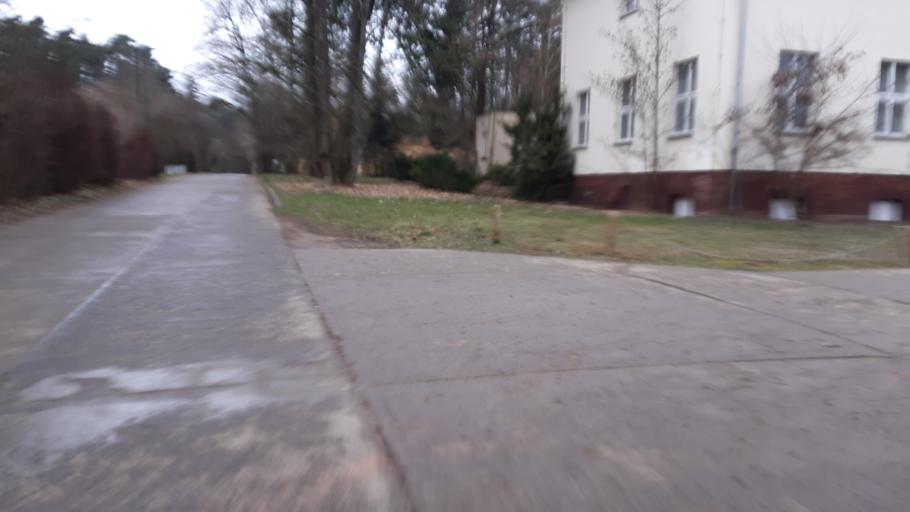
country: DE
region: Brandenburg
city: Templin
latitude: 53.1119
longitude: 13.5317
